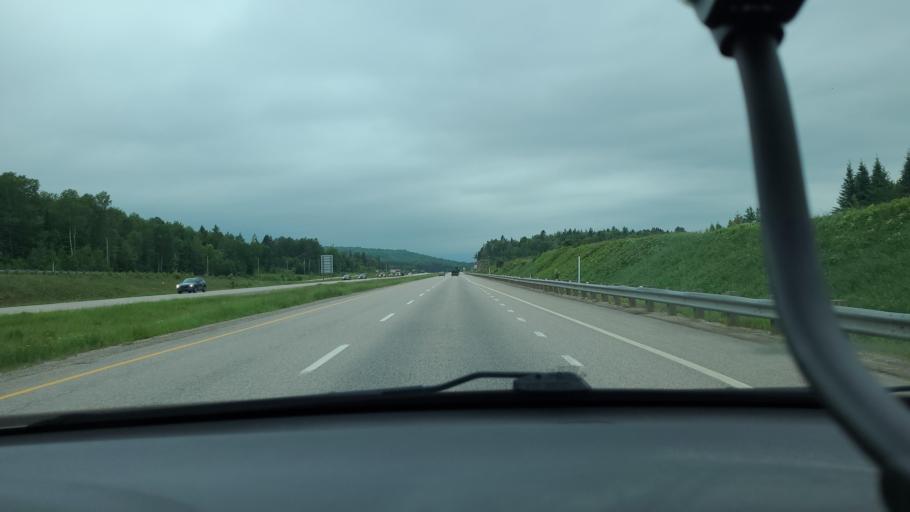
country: CA
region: Quebec
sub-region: Laurentides
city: Labelle
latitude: 46.2795
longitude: -74.7509
